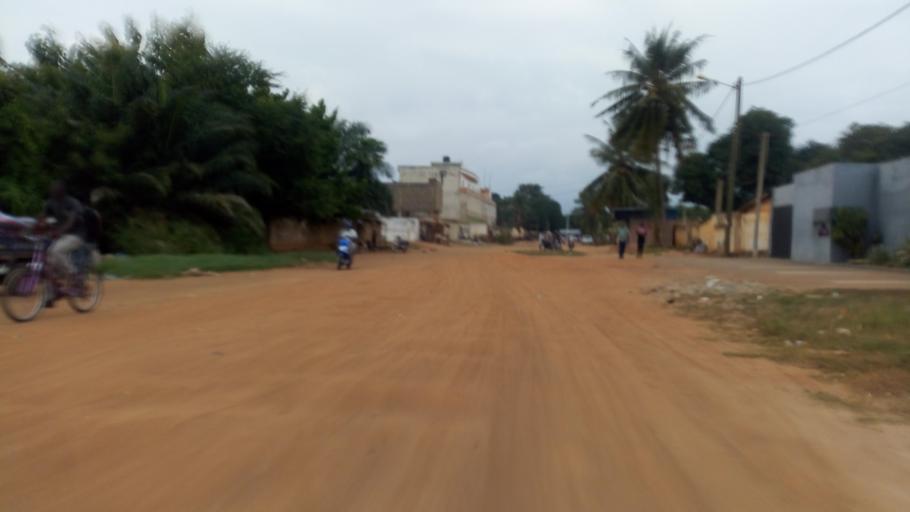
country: TG
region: Maritime
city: Lome
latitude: 6.1794
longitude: 1.1932
